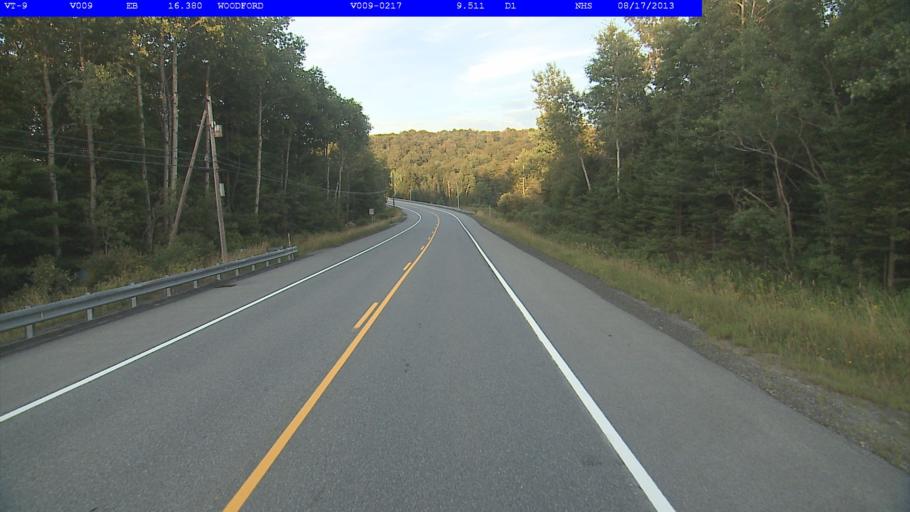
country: US
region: Vermont
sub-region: Bennington County
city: Bennington
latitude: 42.8893
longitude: -73.0115
